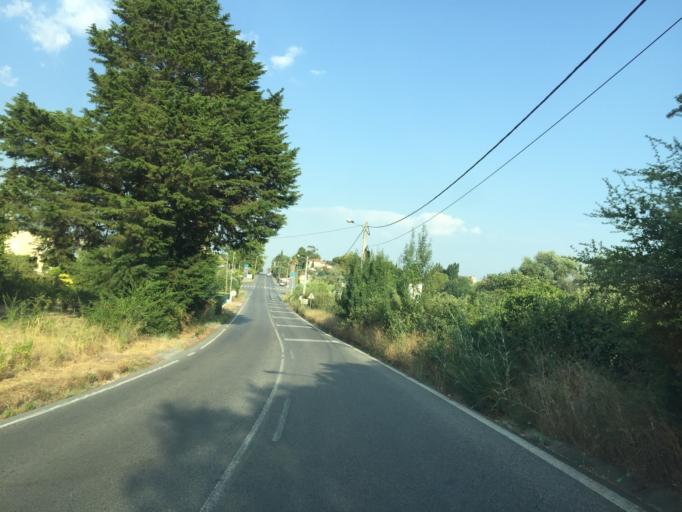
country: PT
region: Santarem
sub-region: Torres Novas
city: Torres Novas
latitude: 39.4770
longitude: -8.5677
